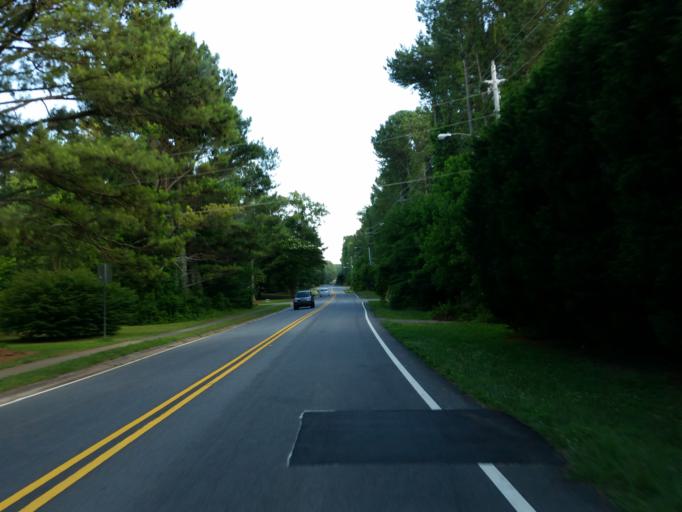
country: US
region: Georgia
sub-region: Cherokee County
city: Woodstock
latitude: 34.0570
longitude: -84.4850
